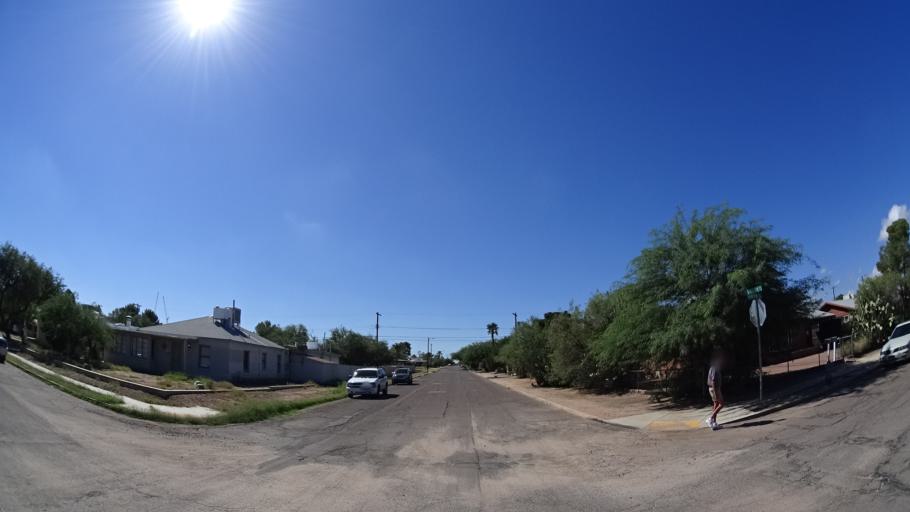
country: US
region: Arizona
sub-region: Pima County
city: Tucson
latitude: 32.2479
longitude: -110.9539
